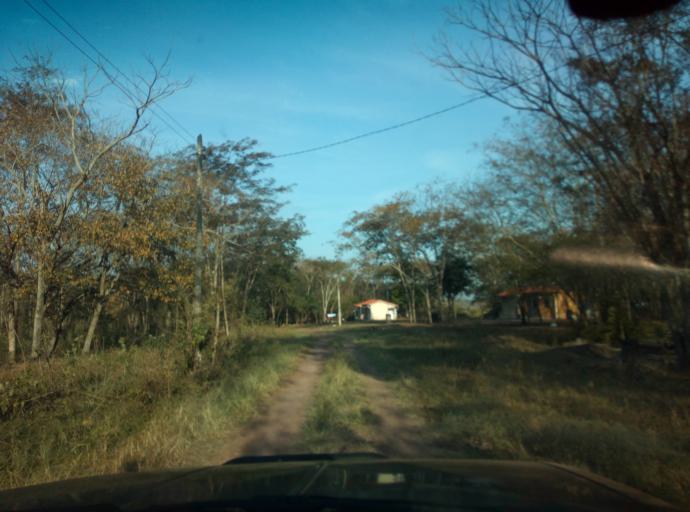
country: PY
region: Caaguazu
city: Doctor Cecilio Baez
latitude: -25.1997
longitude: -56.1354
